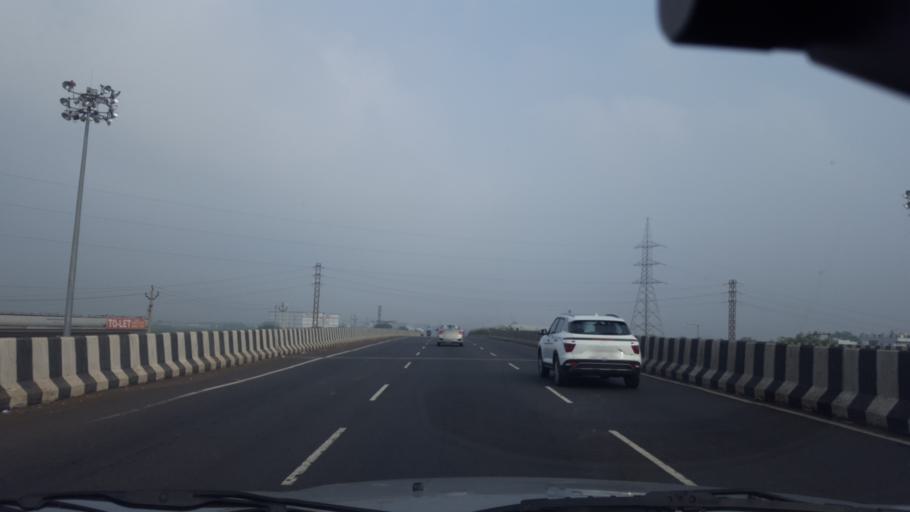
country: IN
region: Andhra Pradesh
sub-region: Prakasam
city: Ongole
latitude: 15.5520
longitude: 80.0560
